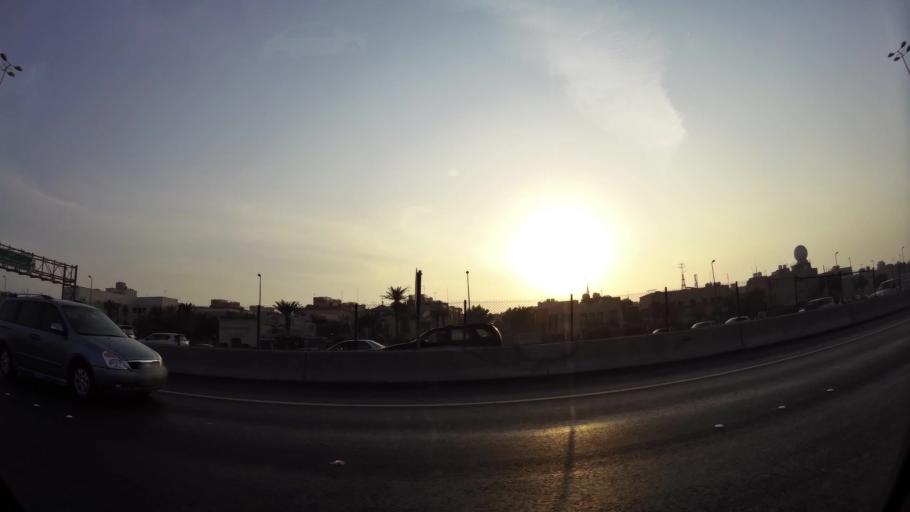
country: KW
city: Bayan
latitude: 29.3202
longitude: 48.0483
